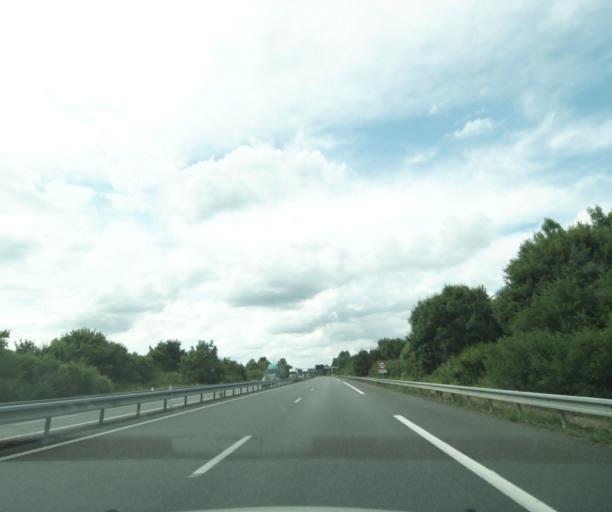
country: FR
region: Centre
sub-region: Departement du Cher
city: Foecy
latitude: 47.1843
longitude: 2.1708
